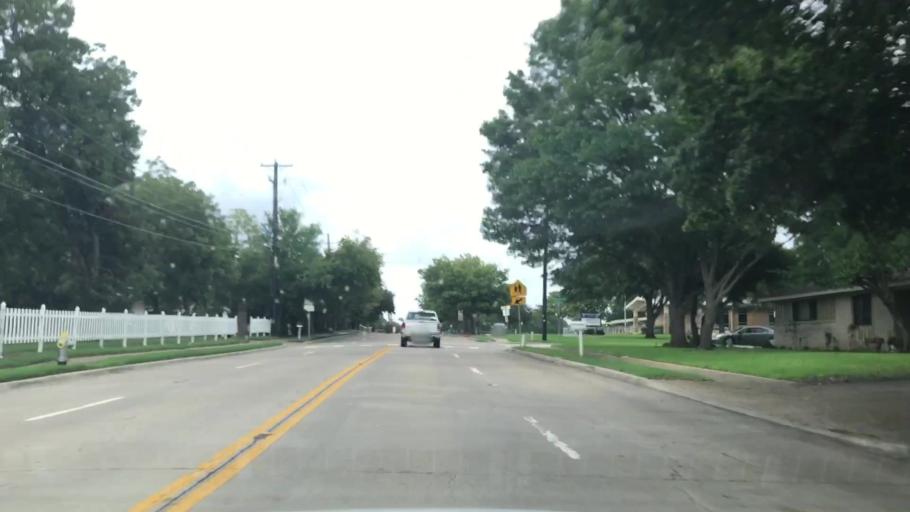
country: US
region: Texas
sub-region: Dallas County
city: Richardson
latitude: 32.9048
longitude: -96.7549
